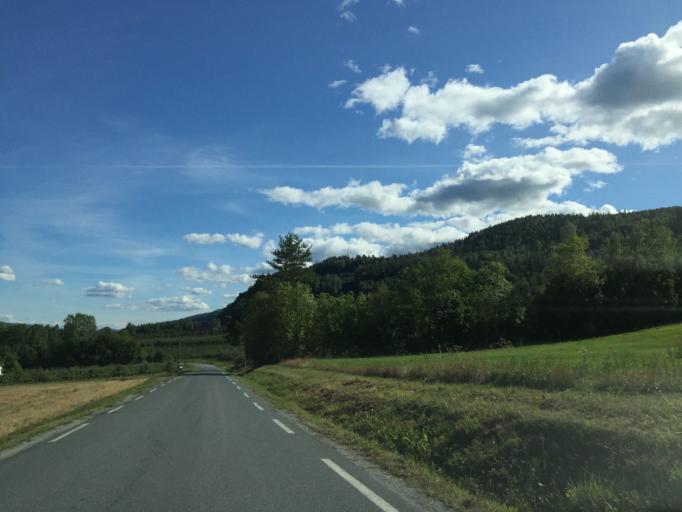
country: NO
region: Buskerud
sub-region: Ovre Eiker
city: Hokksund
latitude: 59.6891
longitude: 9.8478
